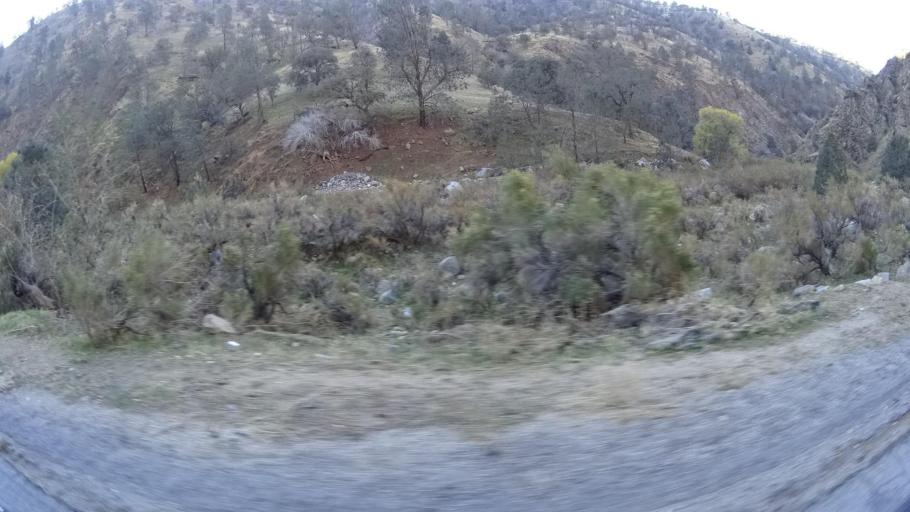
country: US
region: California
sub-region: Kern County
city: Bear Valley Springs
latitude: 35.3169
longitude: -118.5450
